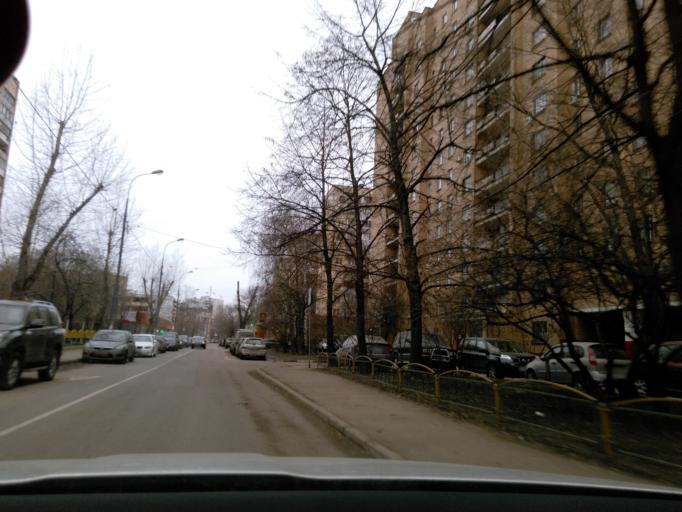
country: RU
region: Moskovskaya
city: Koptevo
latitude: 55.8268
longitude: 37.5207
